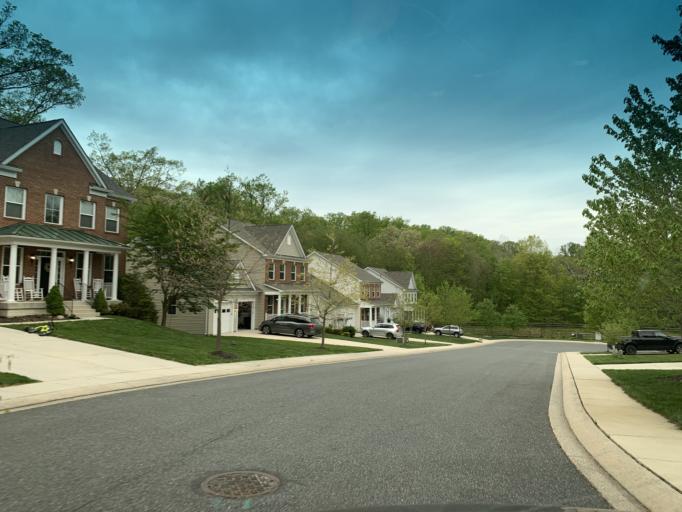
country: US
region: Maryland
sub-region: Harford County
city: South Bel Air
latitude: 39.5249
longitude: -76.3256
